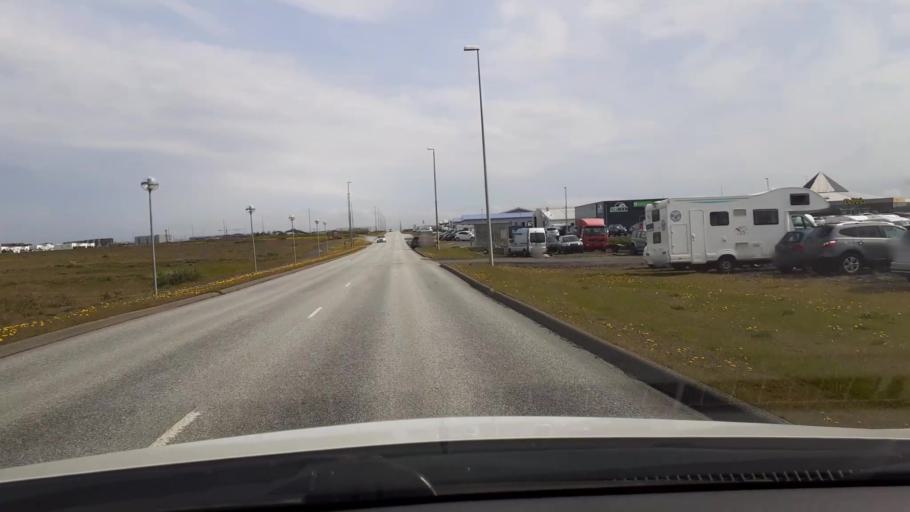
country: IS
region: Southern Peninsula
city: Reykjanesbaer
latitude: 63.9725
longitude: -22.5342
